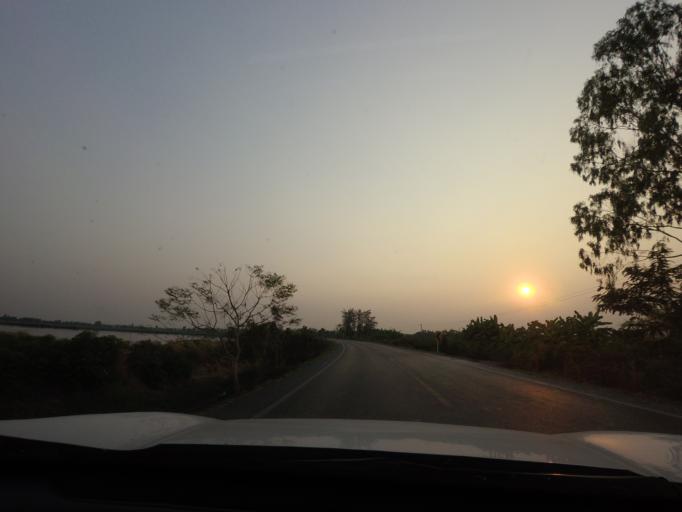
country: TH
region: Nakhon Nayok
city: Ongkharak
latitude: 14.1478
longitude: 101.0337
